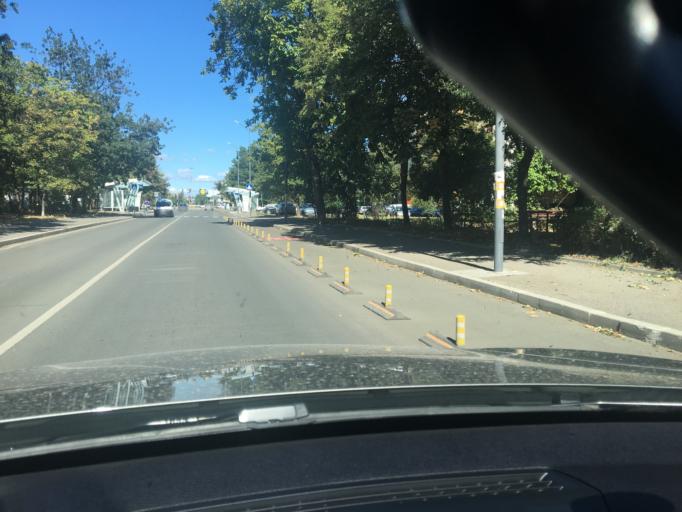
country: BG
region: Burgas
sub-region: Obshtina Burgas
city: Burgas
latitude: 42.5291
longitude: 27.4633
